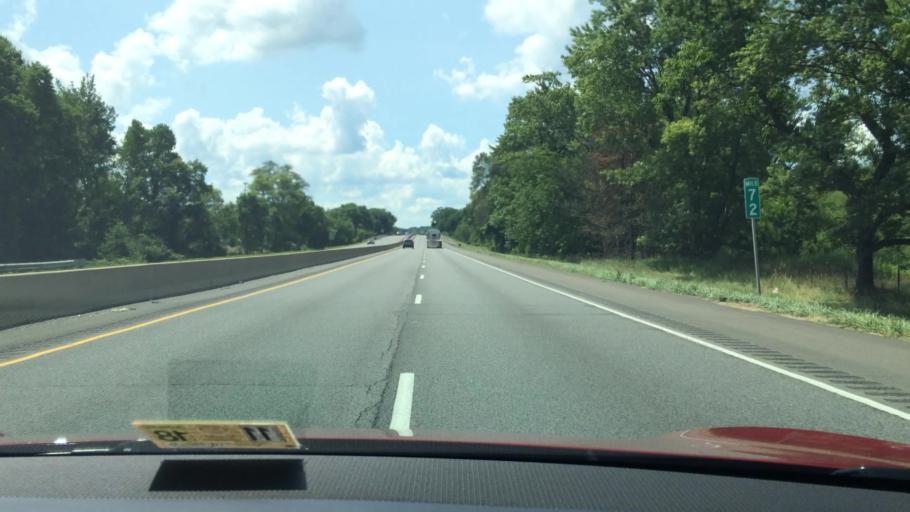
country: US
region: Indiana
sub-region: Saint Joseph County
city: South Bend
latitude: 41.6837
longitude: -86.3410
